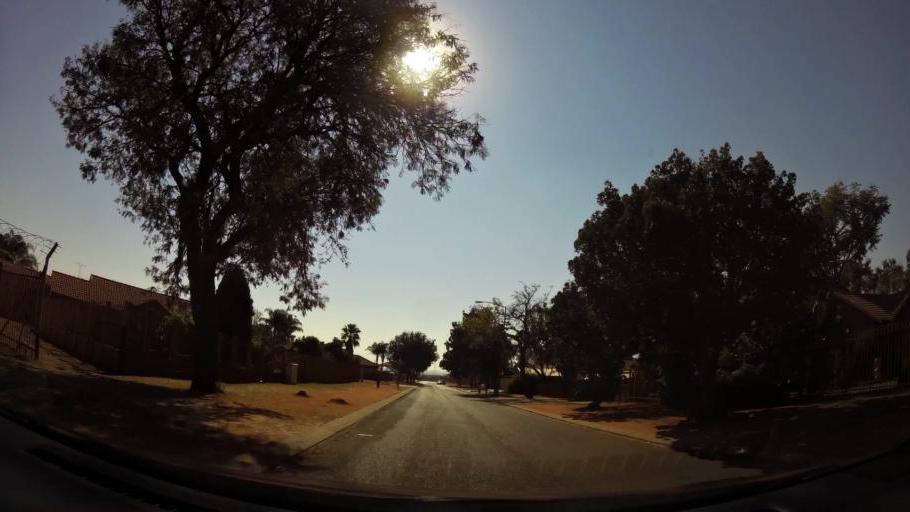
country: ZA
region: North-West
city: Ga-Rankuwa
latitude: -25.6475
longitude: 28.0926
